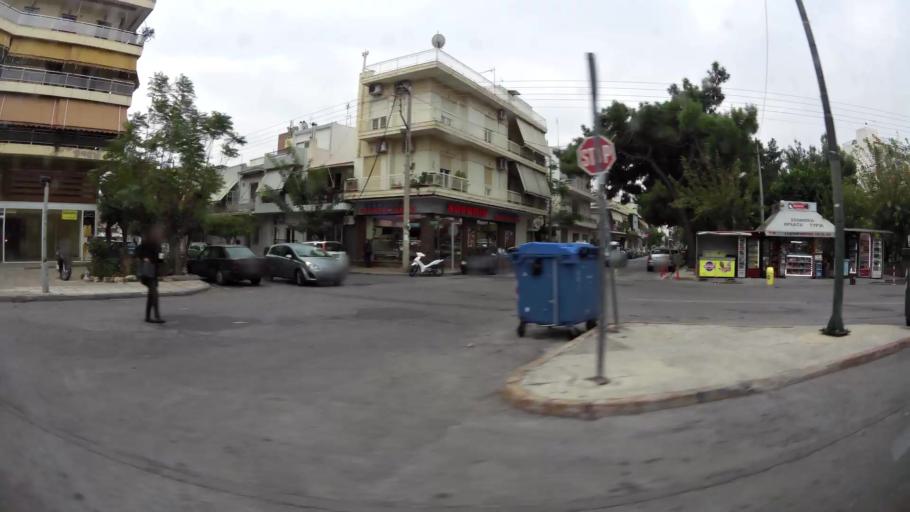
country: GR
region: Attica
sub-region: Nomarchia Athinas
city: Peristeri
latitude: 38.0109
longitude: 23.6995
